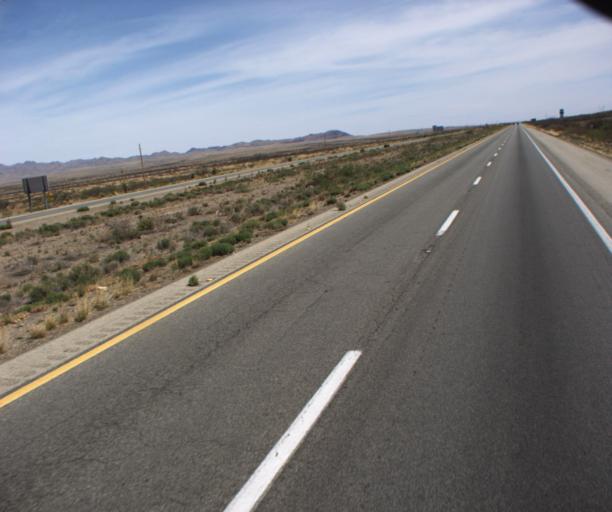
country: US
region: Arizona
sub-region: Cochise County
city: Willcox
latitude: 32.3200
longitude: -109.7811
